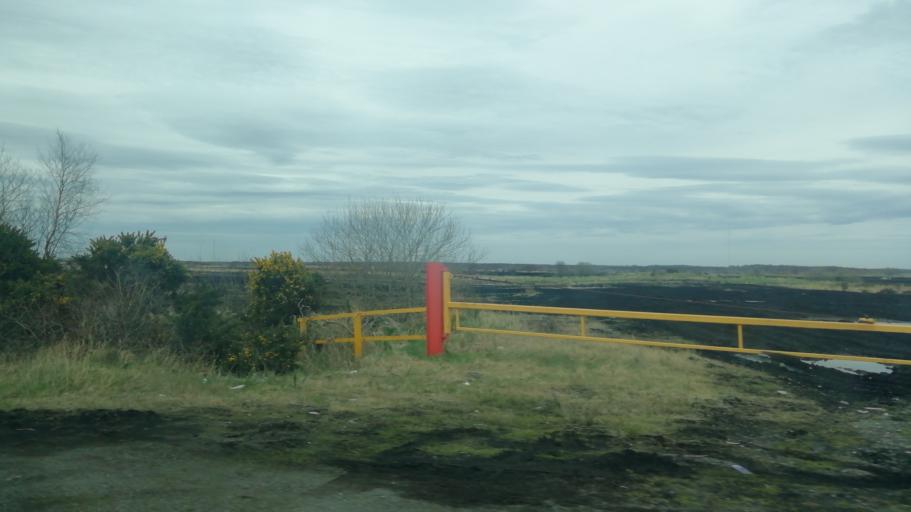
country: IE
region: Leinster
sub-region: Kildare
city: Rathangan
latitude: 53.2559
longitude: -7.0135
